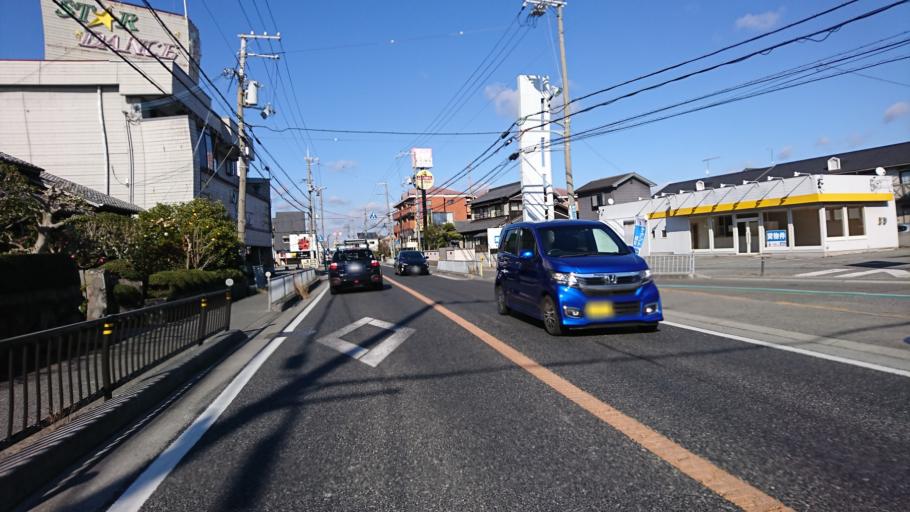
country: JP
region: Hyogo
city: Kakogawacho-honmachi
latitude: 34.7360
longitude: 134.8749
